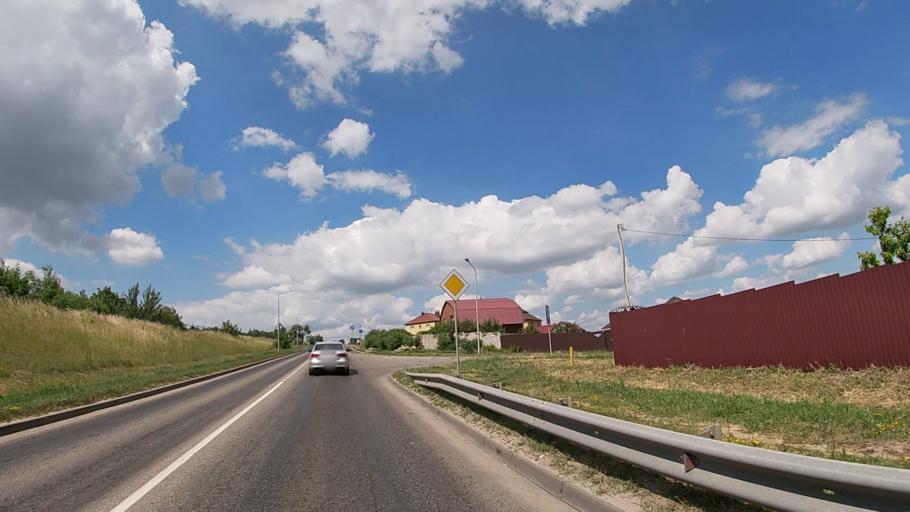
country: RU
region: Belgorod
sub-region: Belgorodskiy Rayon
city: Belgorod
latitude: 50.5950
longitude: 36.5440
